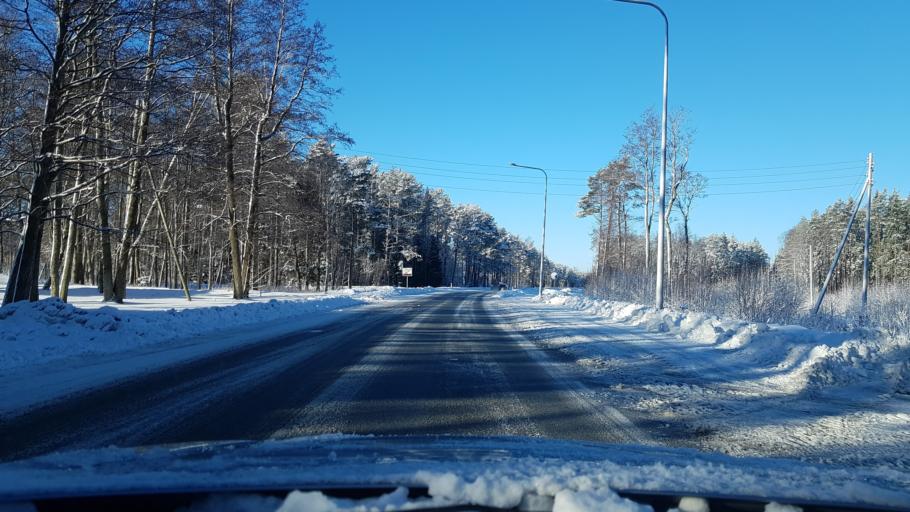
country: EE
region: Hiiumaa
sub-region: Kaerdla linn
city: Kardla
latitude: 58.9949
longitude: 22.7213
